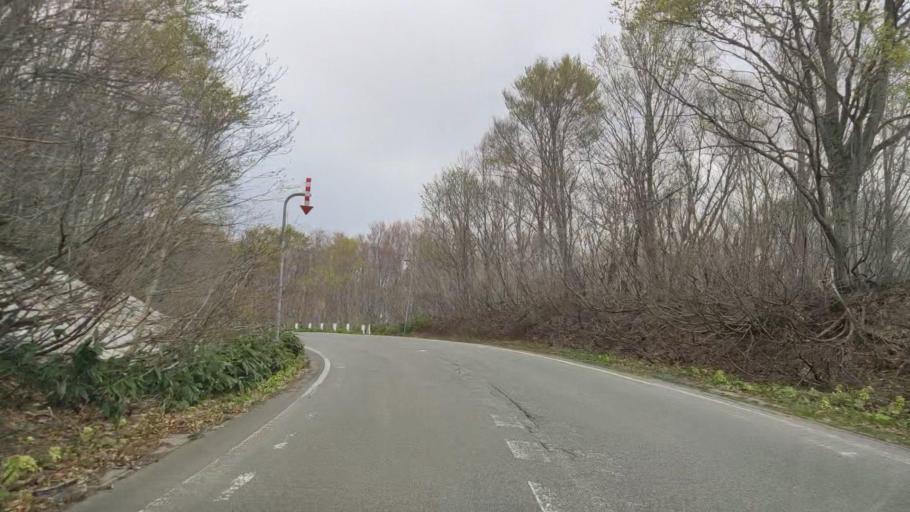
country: JP
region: Aomori
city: Aomori Shi
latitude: 40.6584
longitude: 140.9613
